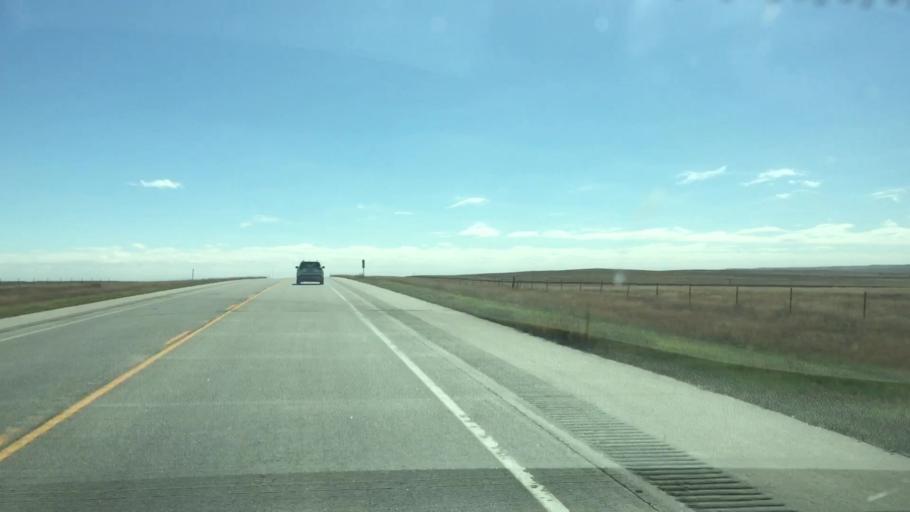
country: US
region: Colorado
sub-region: Lincoln County
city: Hugo
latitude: 39.1803
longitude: -103.5462
